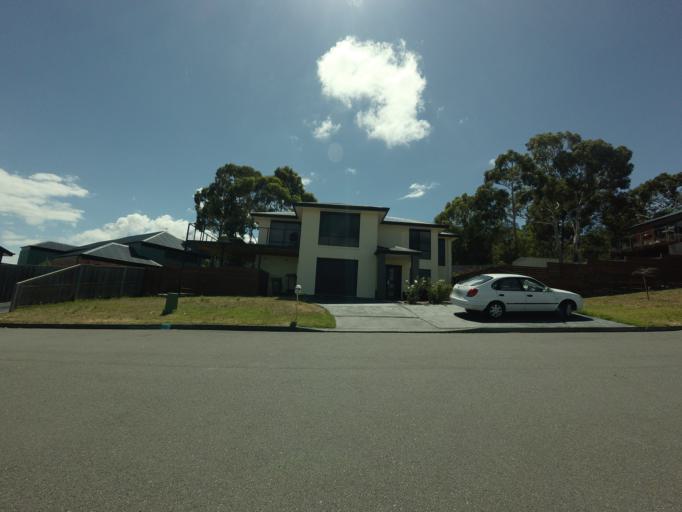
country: AU
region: Tasmania
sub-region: Clarence
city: Rokeby
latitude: -42.8980
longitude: 147.4565
